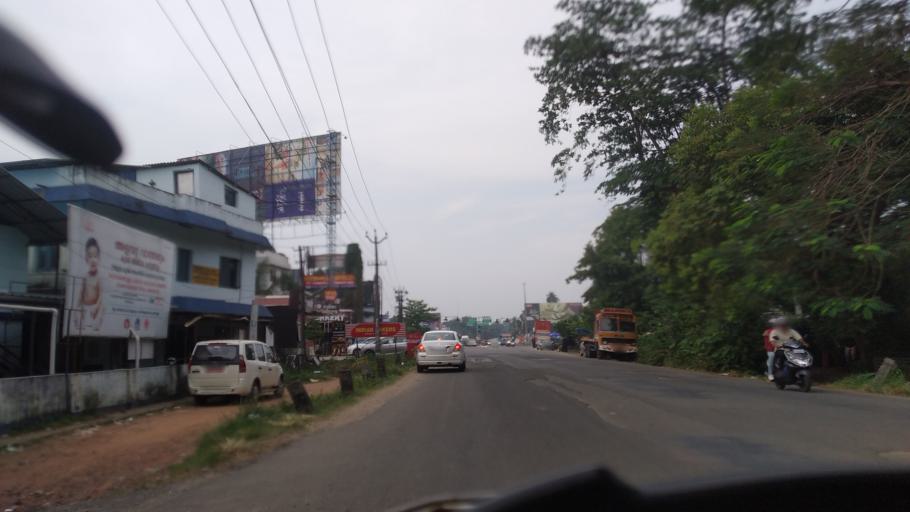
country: IN
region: Kerala
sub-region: Ernakulam
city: Elur
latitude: 10.0600
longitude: 76.2895
